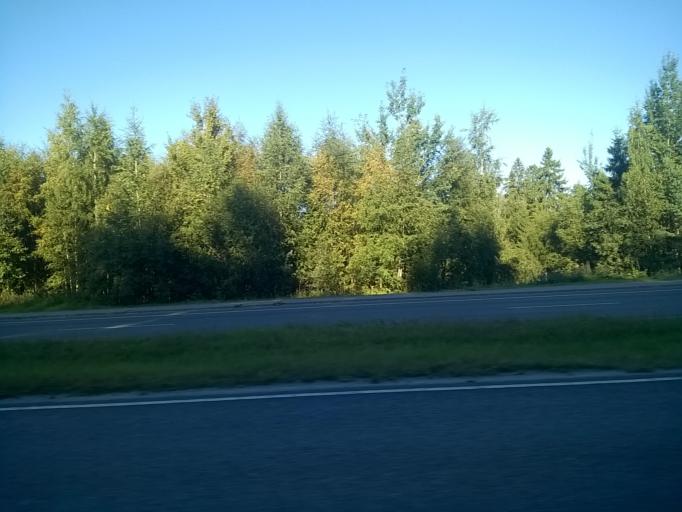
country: FI
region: Pirkanmaa
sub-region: Tampere
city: Tampere
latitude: 61.4607
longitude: 23.8452
